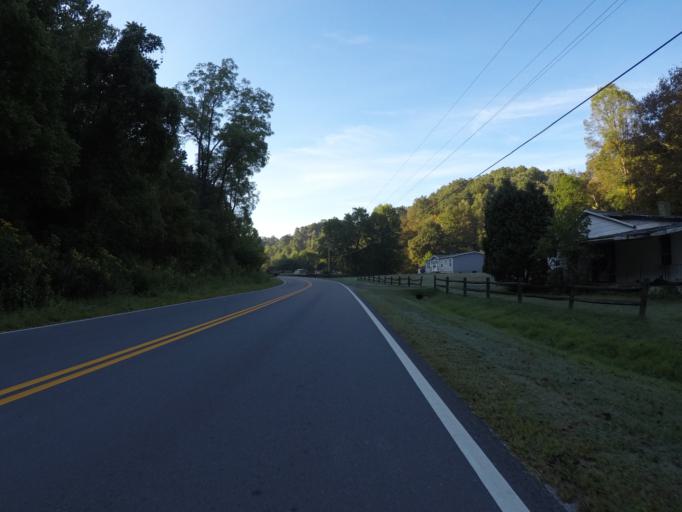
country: US
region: Ohio
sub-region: Lawrence County
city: Ironton
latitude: 38.6121
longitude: -82.5913
